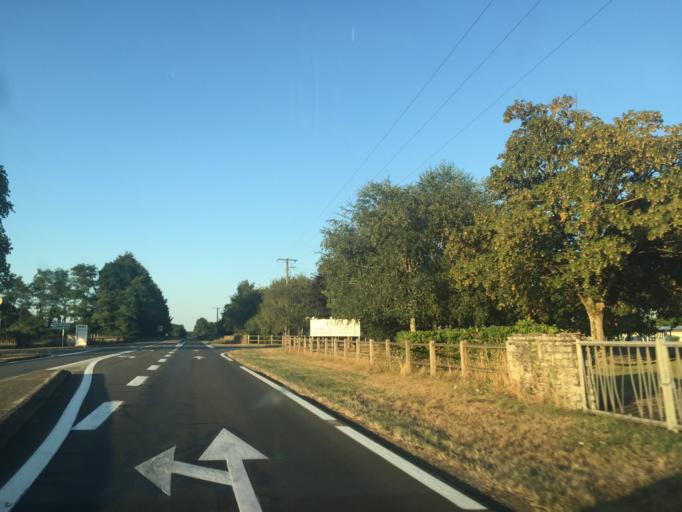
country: FR
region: Poitou-Charentes
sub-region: Departement de la Vienne
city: Rouille
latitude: 46.4036
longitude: 0.0773
